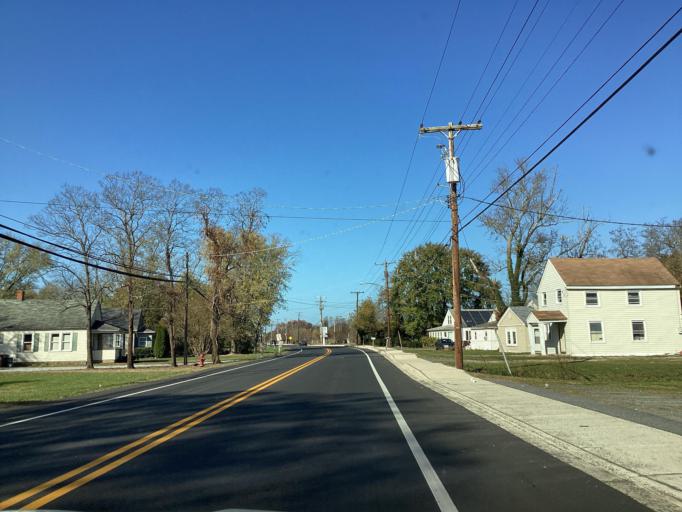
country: US
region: Maryland
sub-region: Dorchester County
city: Cambridge
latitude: 38.5666
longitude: -76.0922
